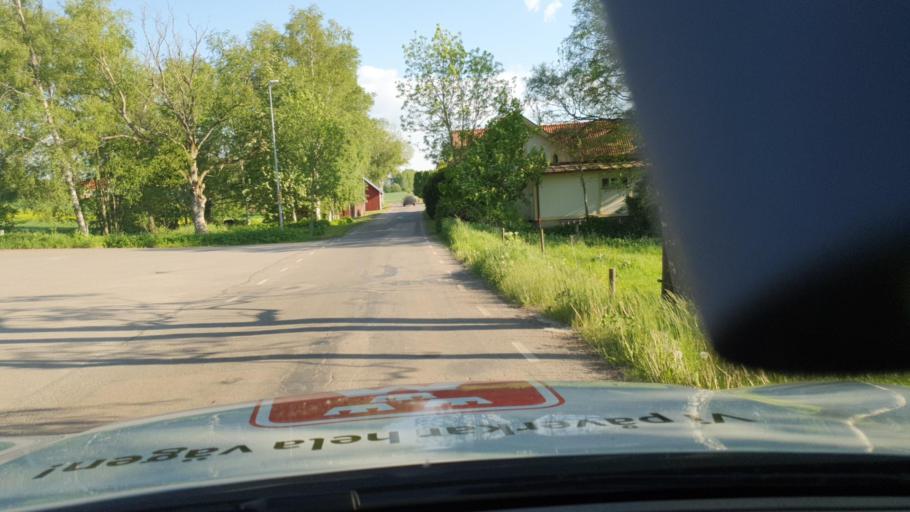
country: SE
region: Vaestra Goetaland
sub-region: Falkopings Kommun
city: Akarp
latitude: 58.1764
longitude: 13.6870
